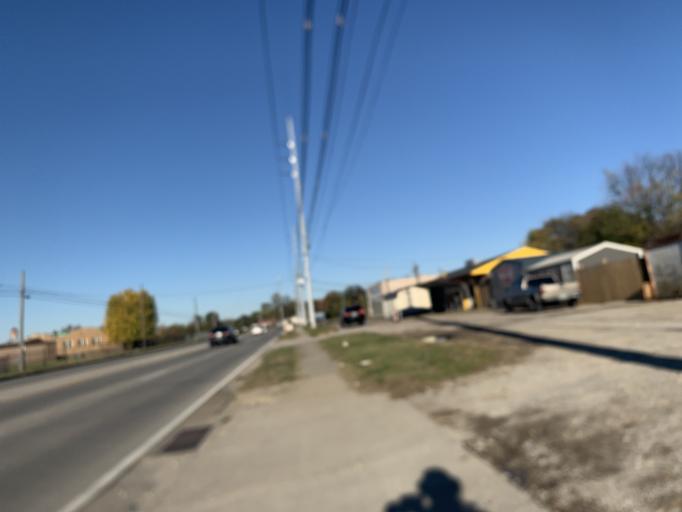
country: US
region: Kentucky
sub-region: Jefferson County
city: Shively
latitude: 38.2014
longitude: -85.7936
